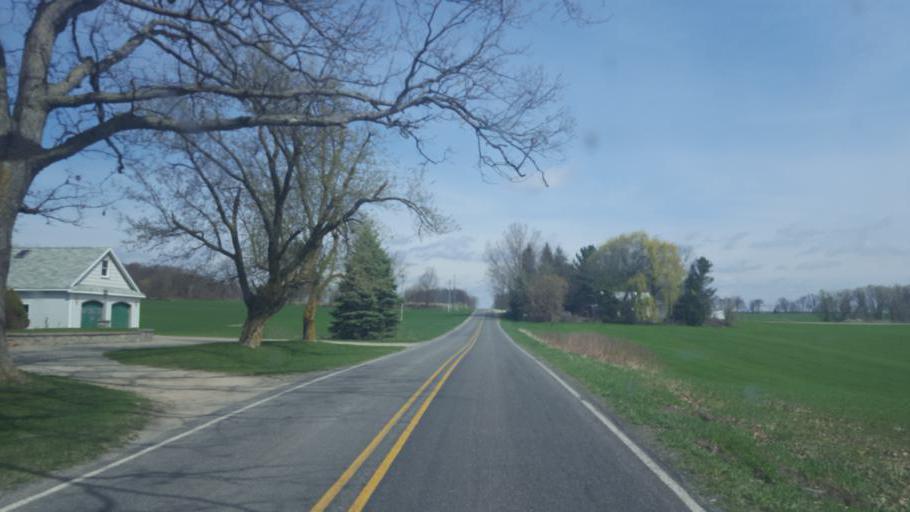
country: US
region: Michigan
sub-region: Montcalm County
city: Edmore
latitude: 43.4421
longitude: -85.0051
